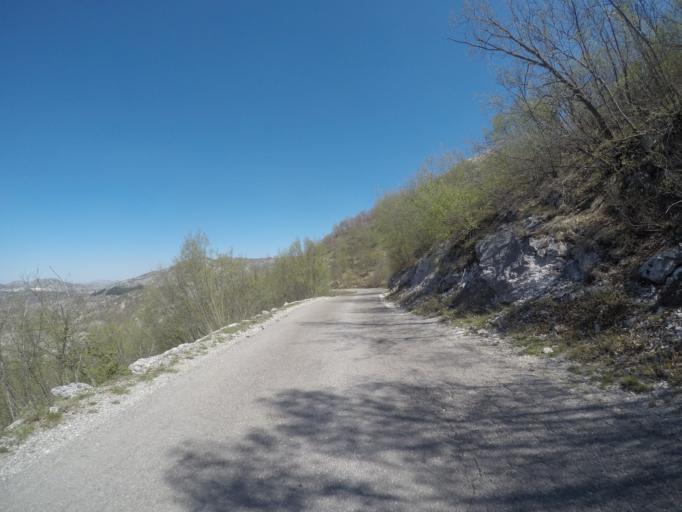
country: ME
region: Cetinje
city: Cetinje
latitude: 42.4482
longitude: 18.8734
